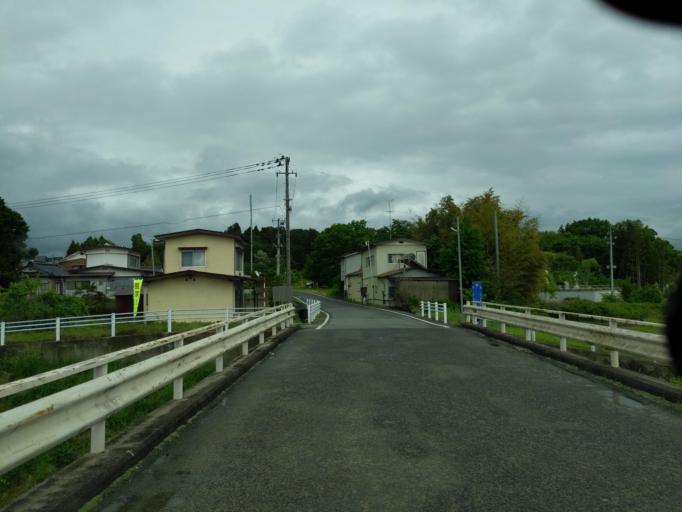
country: JP
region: Fukushima
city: Koriyama
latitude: 37.3582
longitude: 140.3990
